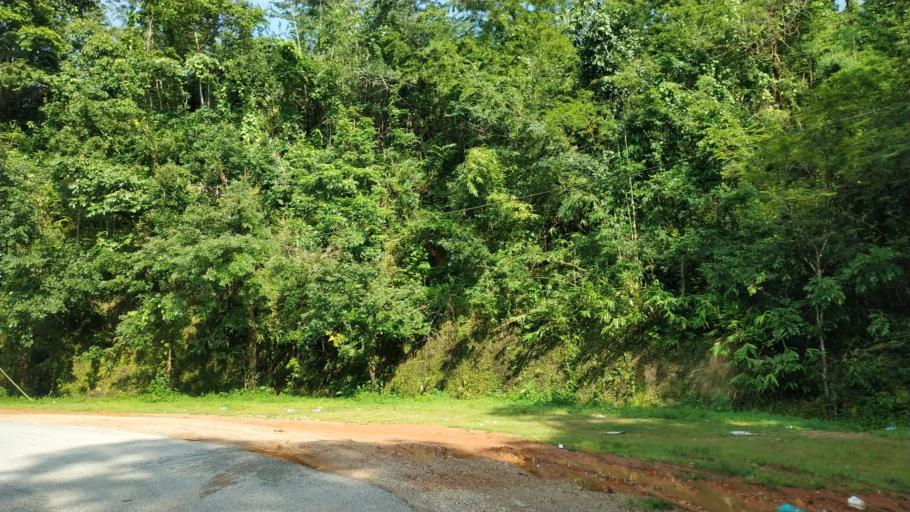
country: TH
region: Kanchanaburi
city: Thong Pha Phum
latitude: 14.6271
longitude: 98.1301
